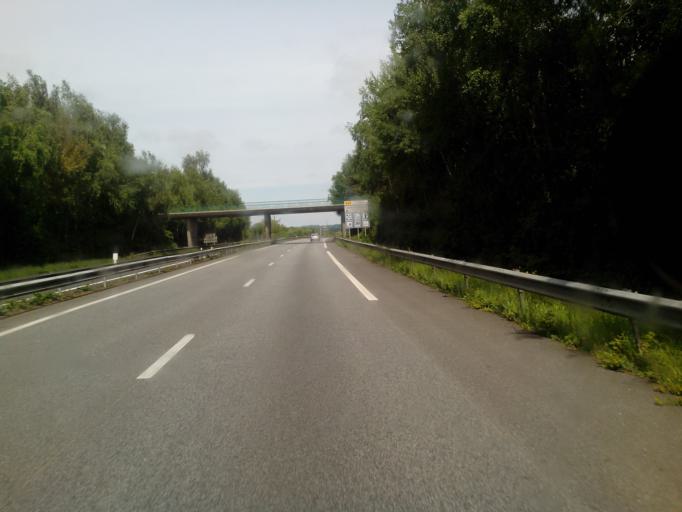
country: FR
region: Pays de la Loire
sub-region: Departement de la Loire-Atlantique
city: Derval
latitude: 47.6870
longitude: -1.6995
